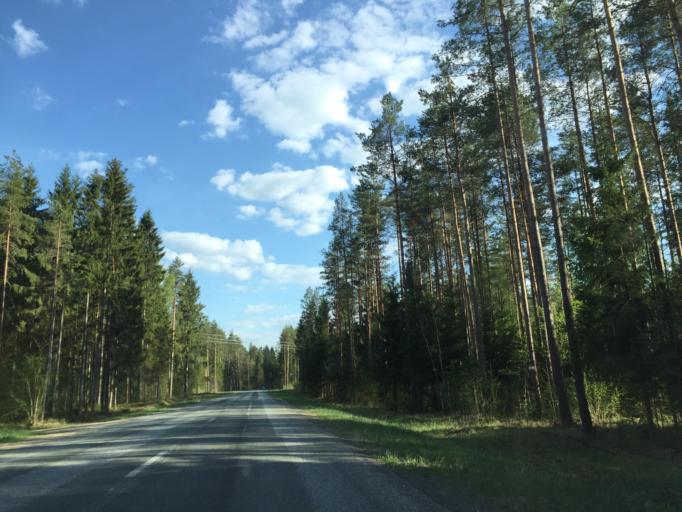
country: LV
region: Sigulda
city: Sigulda
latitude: 57.2240
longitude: 24.8538
